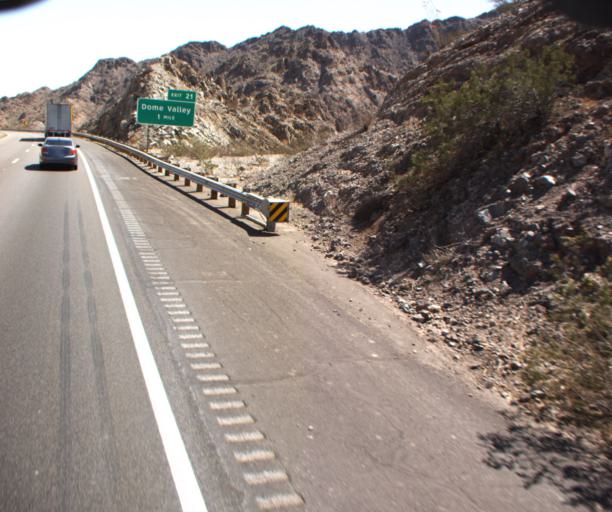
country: US
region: Arizona
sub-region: Yuma County
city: Fortuna Foothills
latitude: 32.6604
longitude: -114.3257
